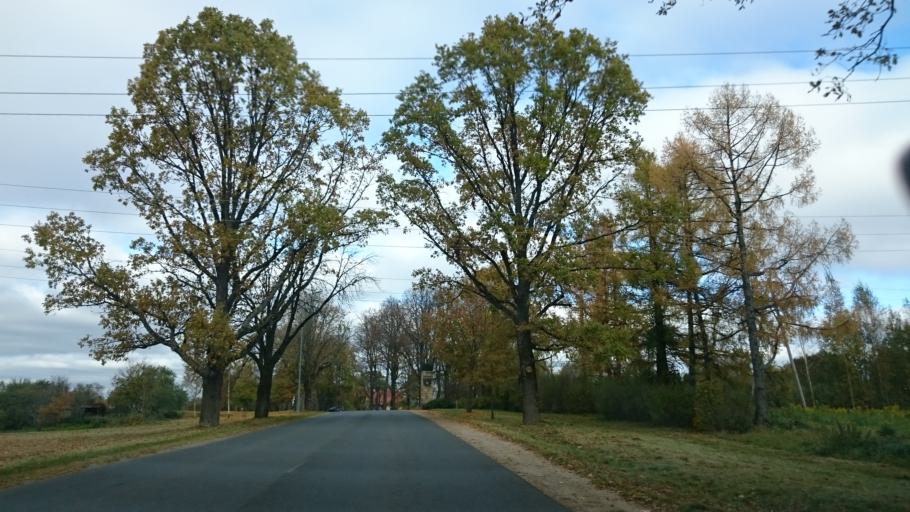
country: LV
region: Cesu Rajons
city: Cesis
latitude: 57.2978
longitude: 25.2691
